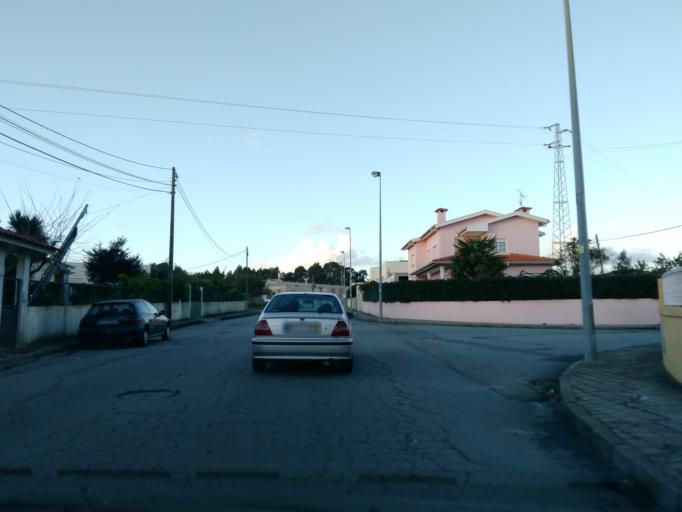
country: PT
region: Braga
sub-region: Braga
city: Braga
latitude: 41.5287
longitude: -8.4546
